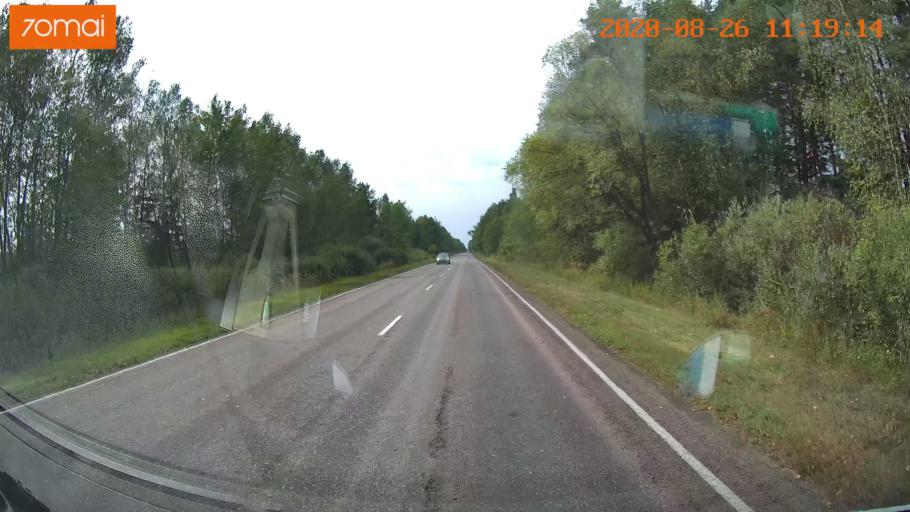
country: RU
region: Rjazan
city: Shilovo
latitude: 54.4014
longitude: 41.0832
